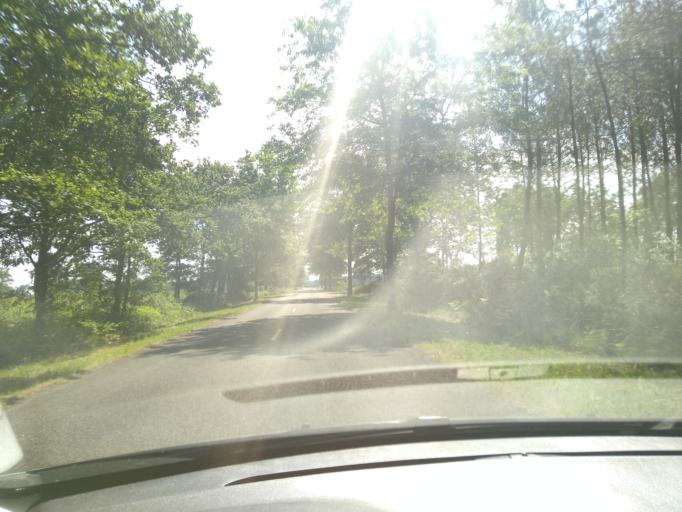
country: FR
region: Aquitaine
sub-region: Departement des Landes
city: Saint-Vincent-de-Paul
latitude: 43.7841
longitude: -0.9811
